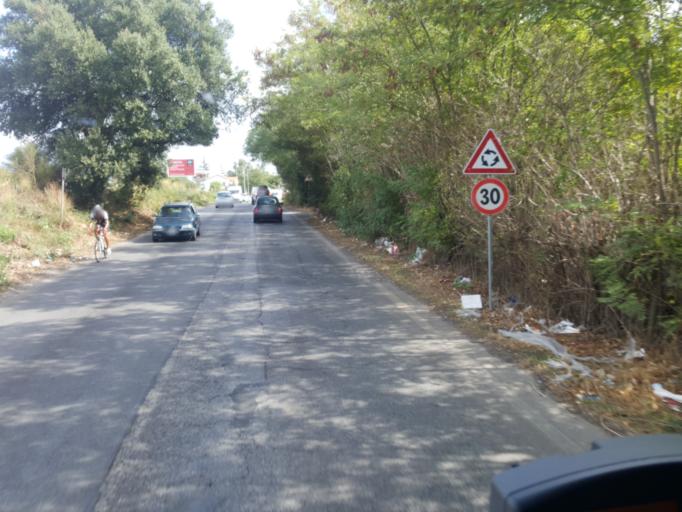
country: IT
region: Latium
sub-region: Citta metropolitana di Roma Capitale
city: Area Produttiva
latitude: 41.6940
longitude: 12.5220
